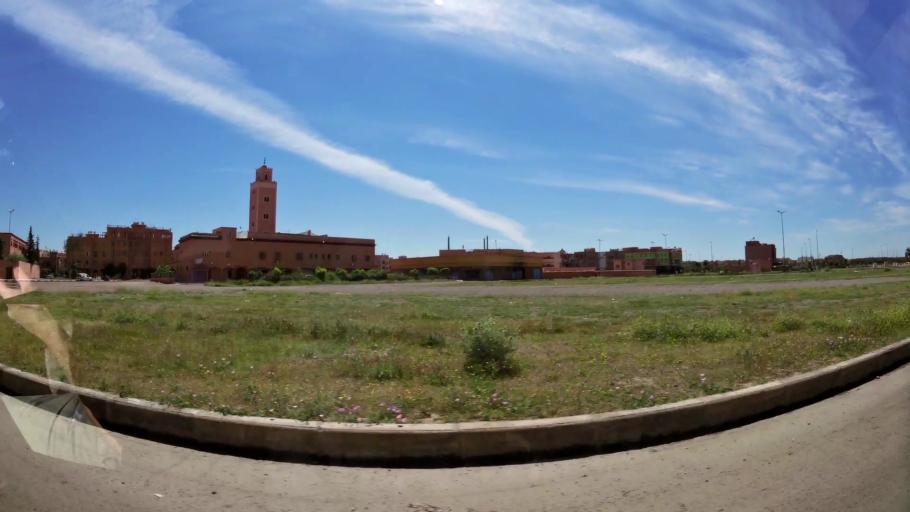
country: MA
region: Marrakech-Tensift-Al Haouz
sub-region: Marrakech
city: Marrakesh
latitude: 31.6488
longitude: -8.0650
